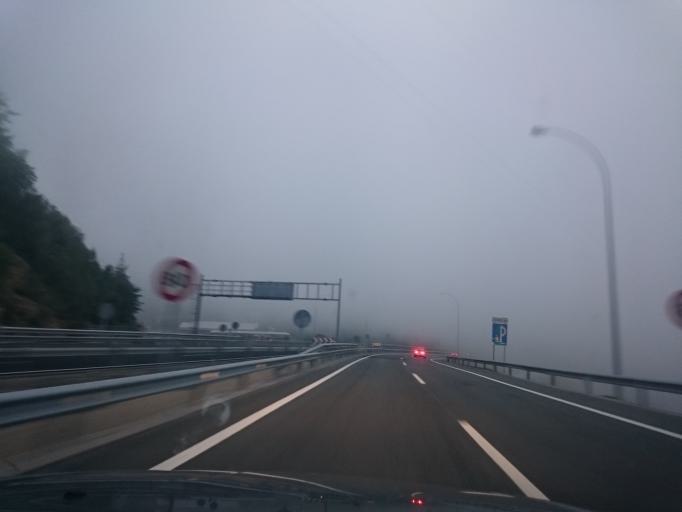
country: ES
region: Castille and Leon
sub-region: Provincia de Leon
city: Sena de Luna
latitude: 42.9801
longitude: -5.8310
